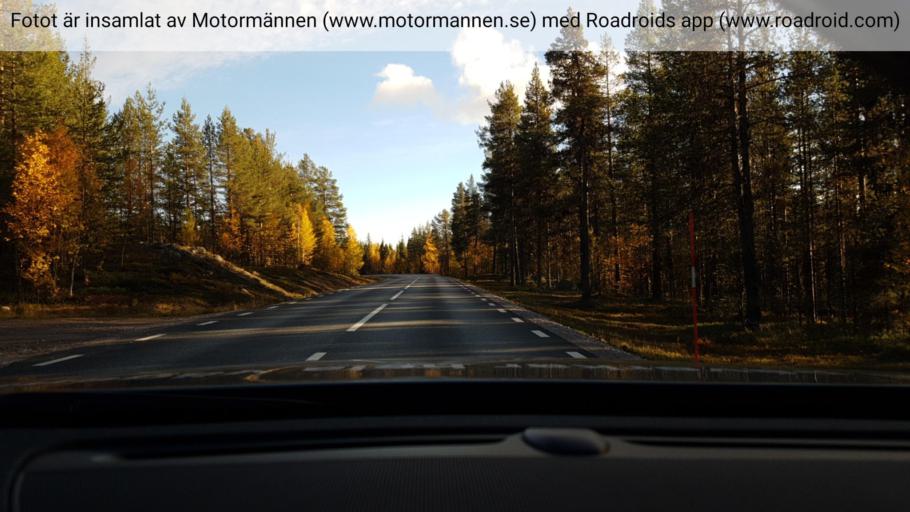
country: SE
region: Norrbotten
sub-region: Jokkmokks Kommun
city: Jokkmokk
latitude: 66.9215
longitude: 19.8282
